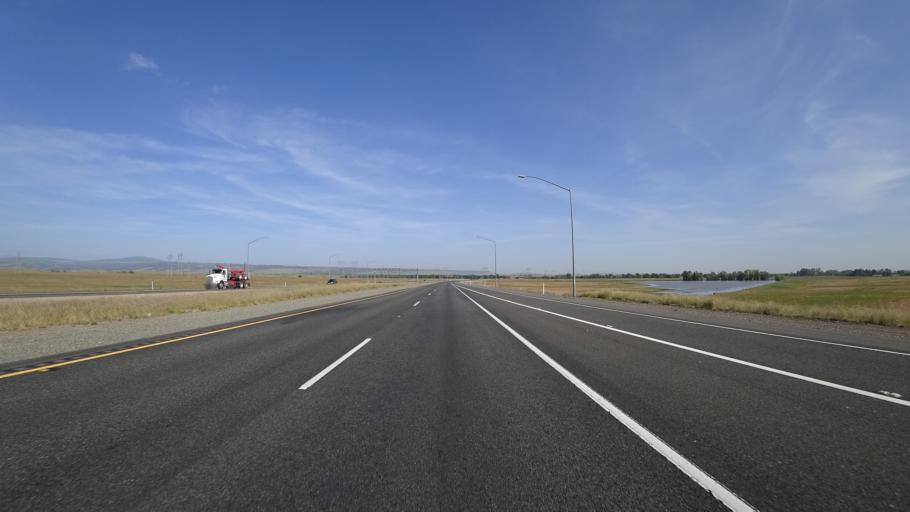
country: US
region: California
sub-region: Butte County
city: Durham
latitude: 39.6179
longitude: -121.6864
